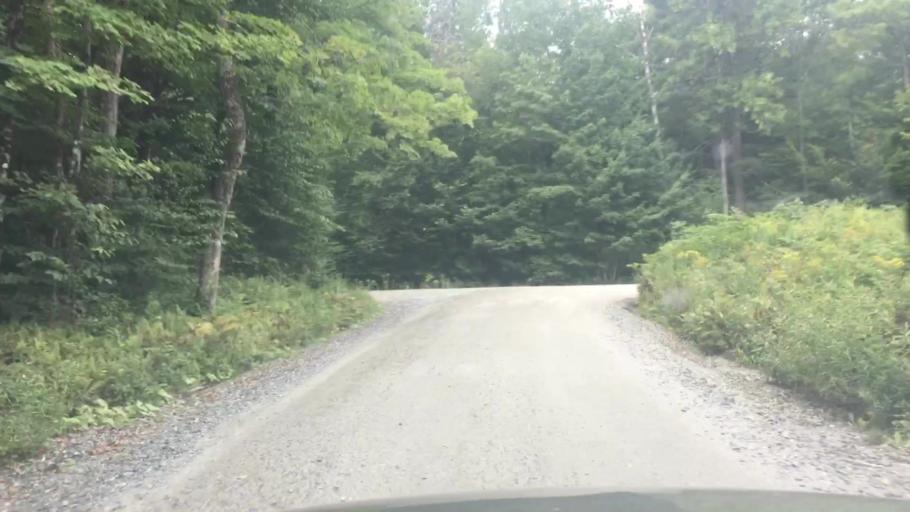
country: US
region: Vermont
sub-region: Windham County
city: Dover
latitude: 42.8220
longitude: -72.7808
